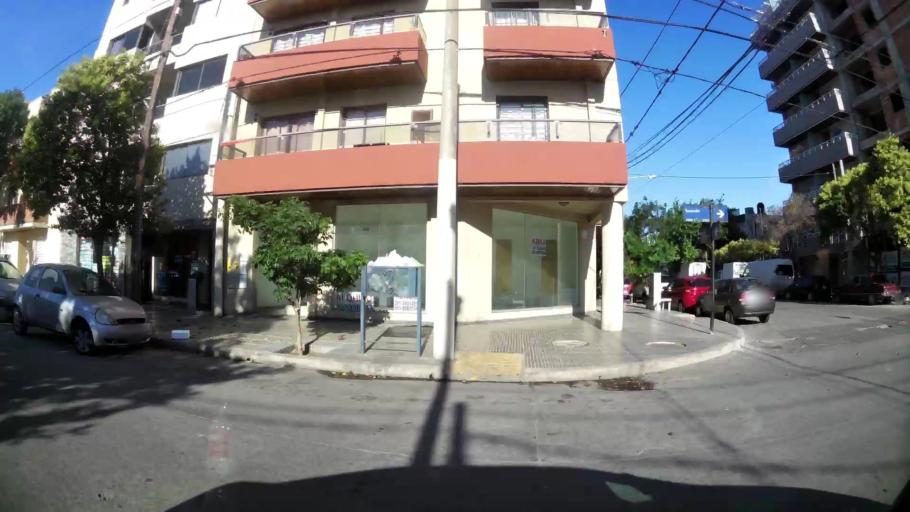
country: AR
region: Cordoba
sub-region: Departamento de Capital
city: Cordoba
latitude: -31.3899
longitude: -64.1783
